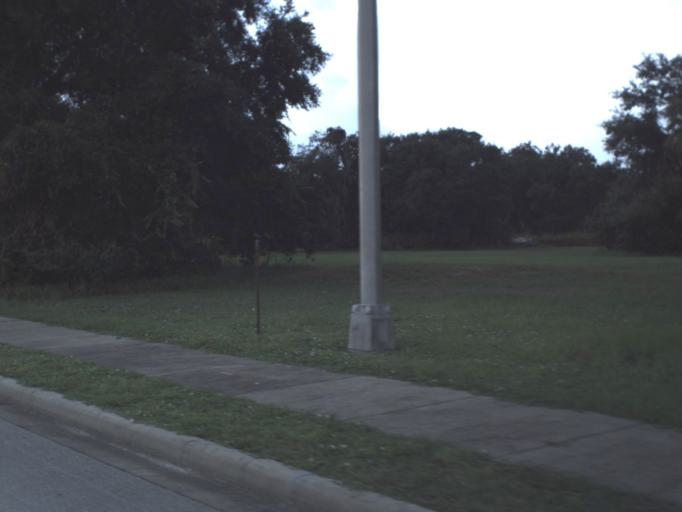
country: US
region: Florida
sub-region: Charlotte County
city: Cleveland
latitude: 26.9696
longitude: -81.9636
